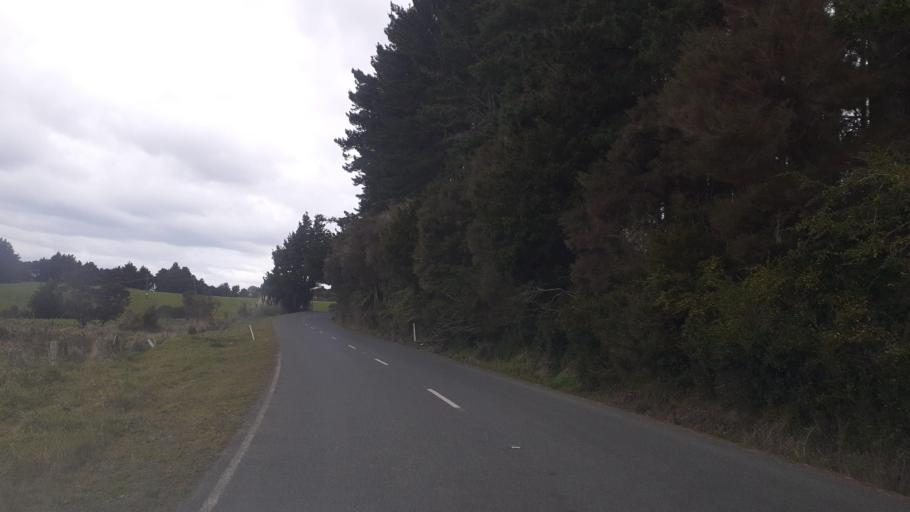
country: NZ
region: Northland
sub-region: Far North District
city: Moerewa
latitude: -35.5883
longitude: 173.9731
